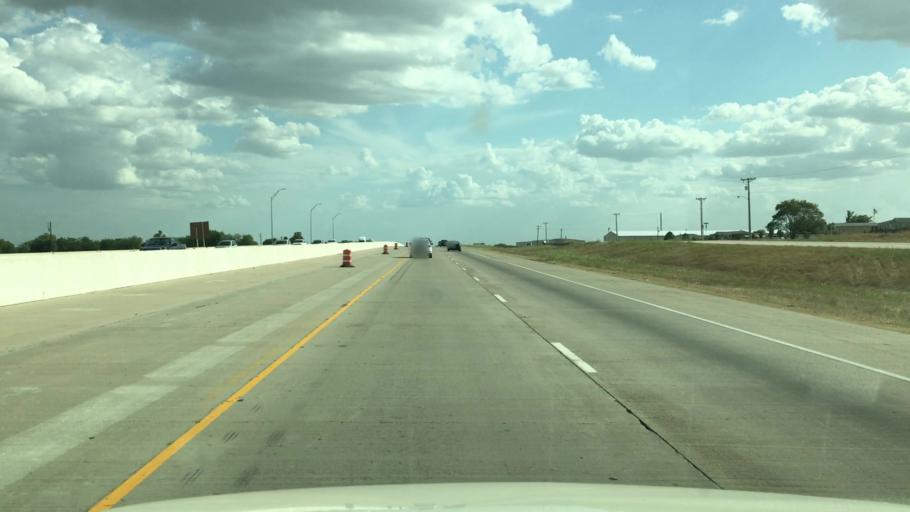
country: US
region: Texas
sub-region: McLennan County
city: Bruceville-Eddy
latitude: 31.2563
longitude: -97.2755
